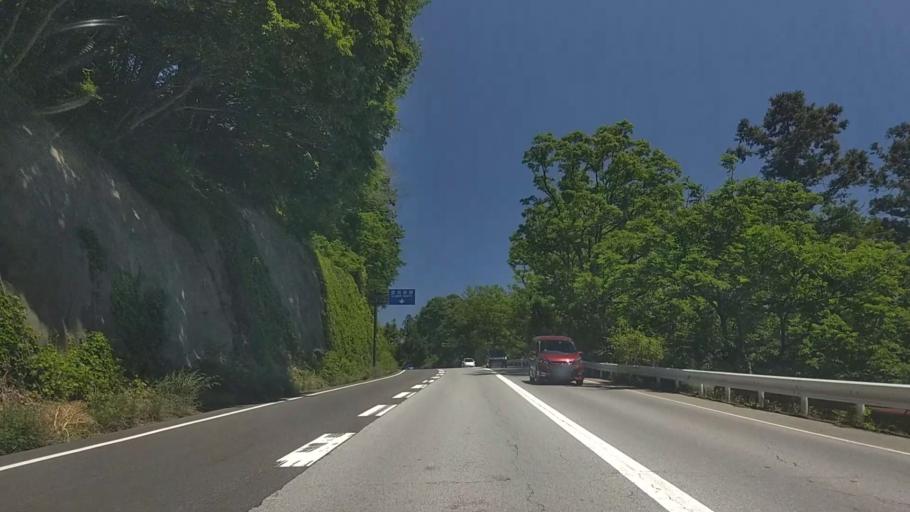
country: JP
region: Yamanashi
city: Nirasaki
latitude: 35.8047
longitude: 138.4272
